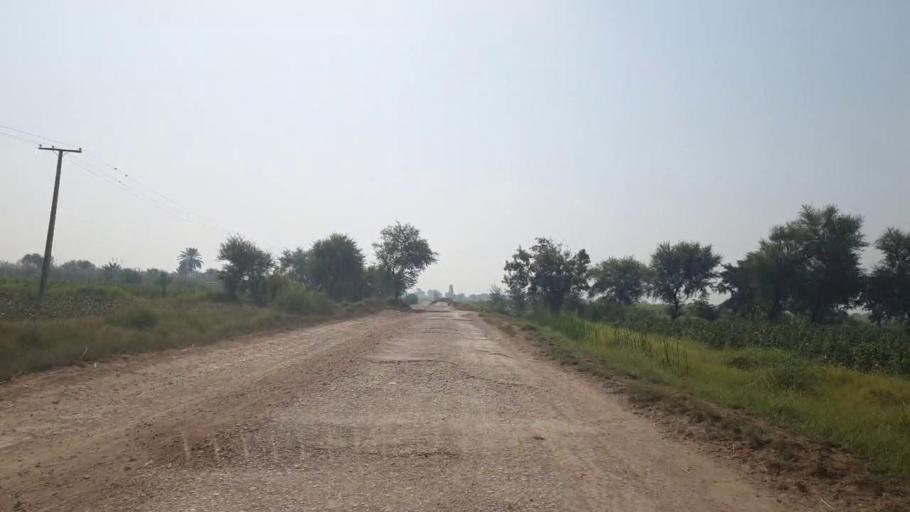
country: PK
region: Sindh
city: Shahdadpur
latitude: 25.9159
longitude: 68.7389
